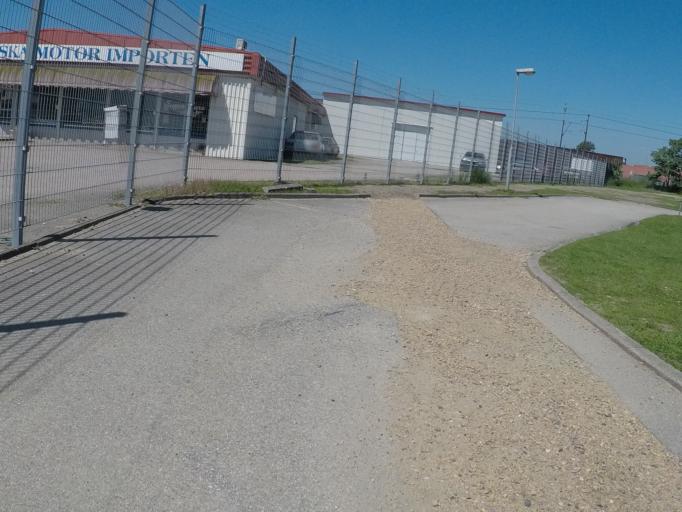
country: SE
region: Skane
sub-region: Burlovs Kommun
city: Arloev
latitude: 55.6396
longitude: 13.0799
